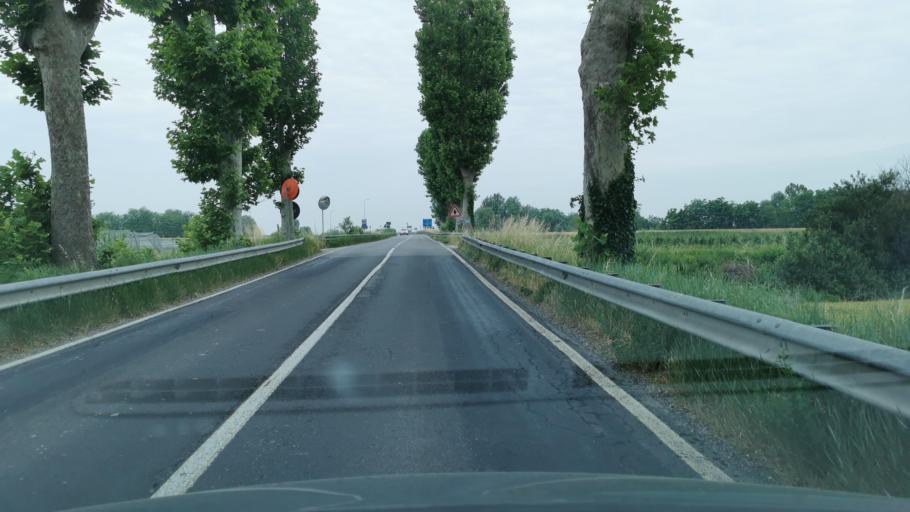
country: IT
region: Emilia-Romagna
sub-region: Provincia di Ravenna
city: Russi
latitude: 44.4003
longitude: 12.0267
